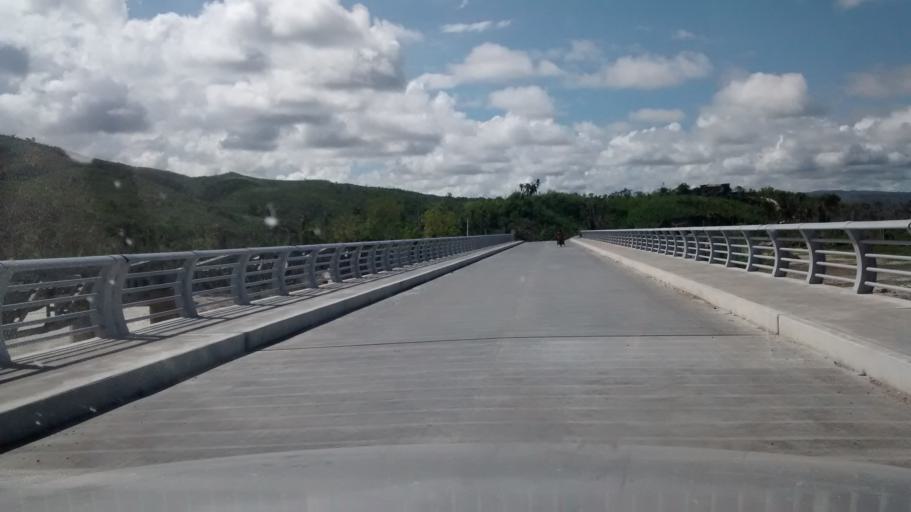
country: HT
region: Grandans
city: Jeremie
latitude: 18.5976
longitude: -74.0308
